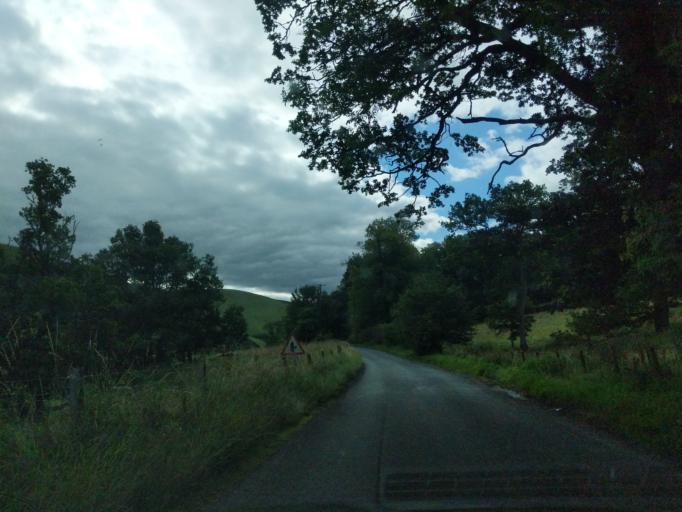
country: GB
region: Scotland
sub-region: The Scottish Borders
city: West Linton
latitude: 55.7006
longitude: -3.3390
